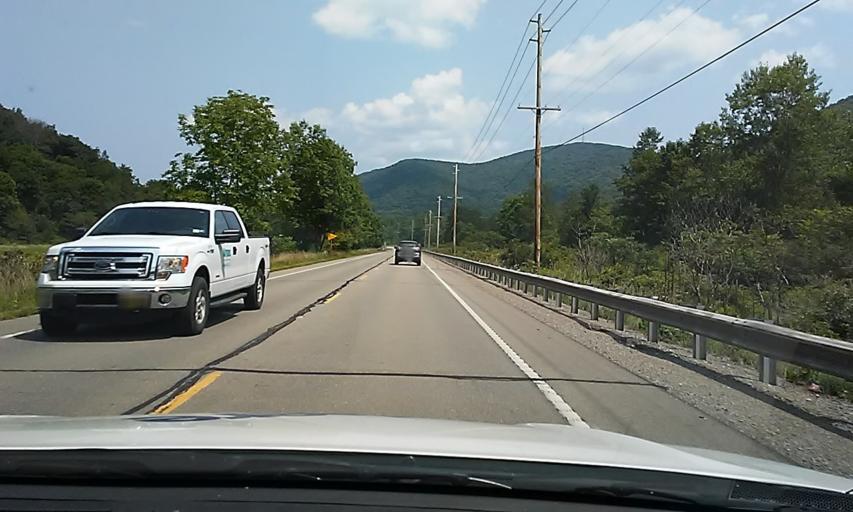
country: US
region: Pennsylvania
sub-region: Cameron County
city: Emporium
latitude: 41.4924
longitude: -78.2849
